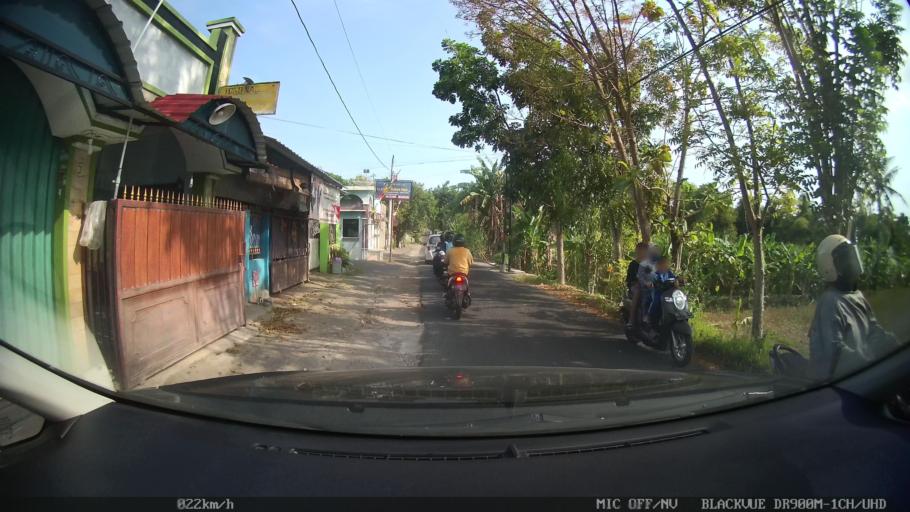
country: ID
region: Daerah Istimewa Yogyakarta
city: Kasihan
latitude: -7.8306
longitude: 110.3236
